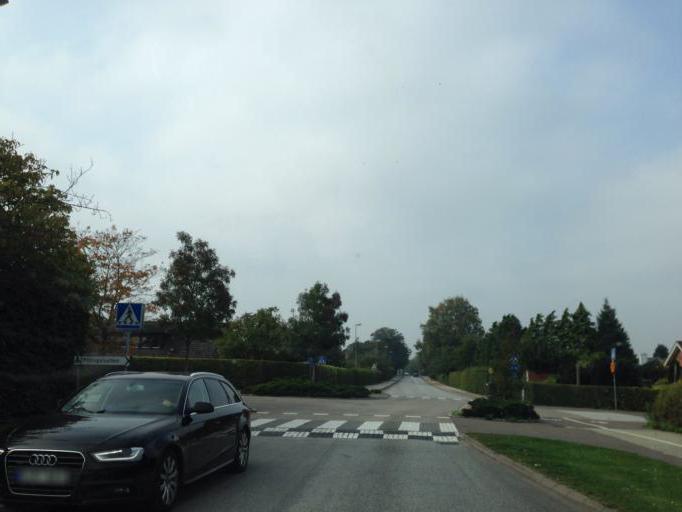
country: SE
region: Skane
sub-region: Lomma Kommun
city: Lomma
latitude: 55.6679
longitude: 13.0830
